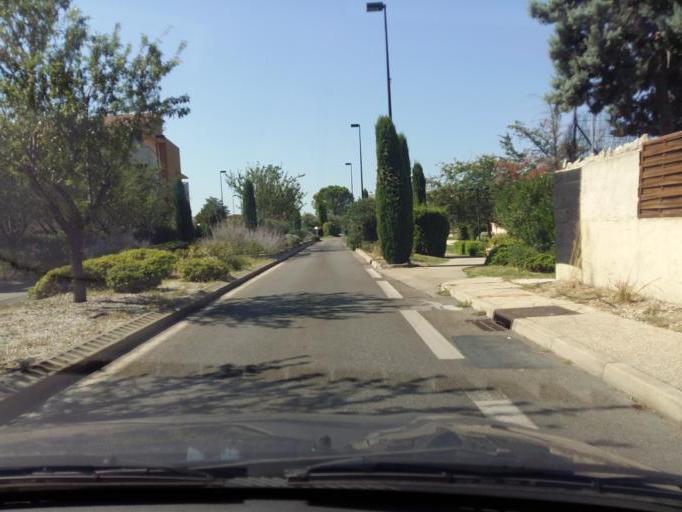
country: FR
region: Languedoc-Roussillon
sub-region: Departement du Gard
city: Les Angles
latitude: 43.9584
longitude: 4.7670
